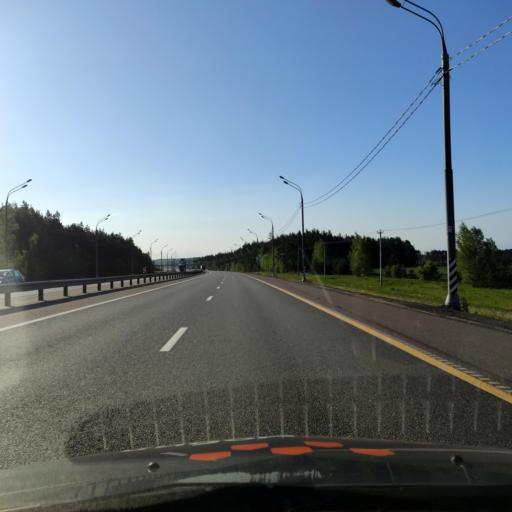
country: RU
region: Lipetsk
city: Zadonsk
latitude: 52.3795
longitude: 38.8801
